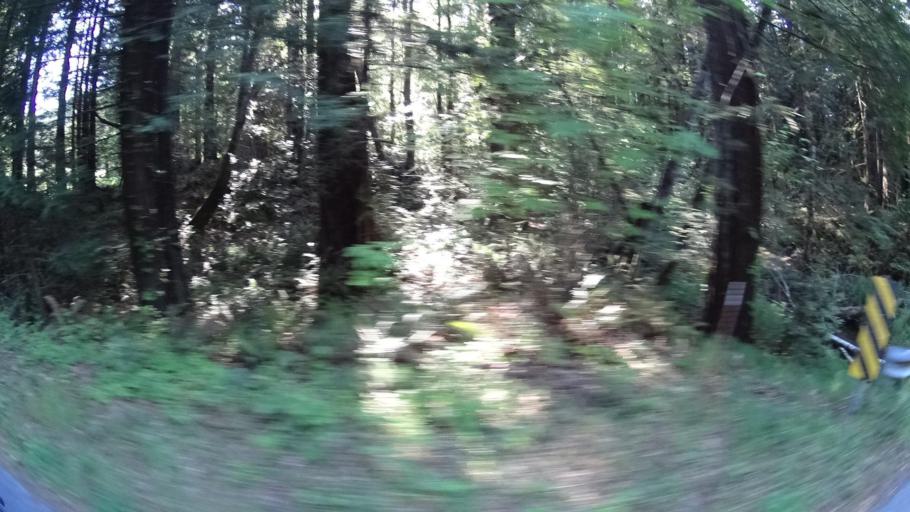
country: US
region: California
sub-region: Humboldt County
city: Rio Dell
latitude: 40.4354
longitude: -123.9642
